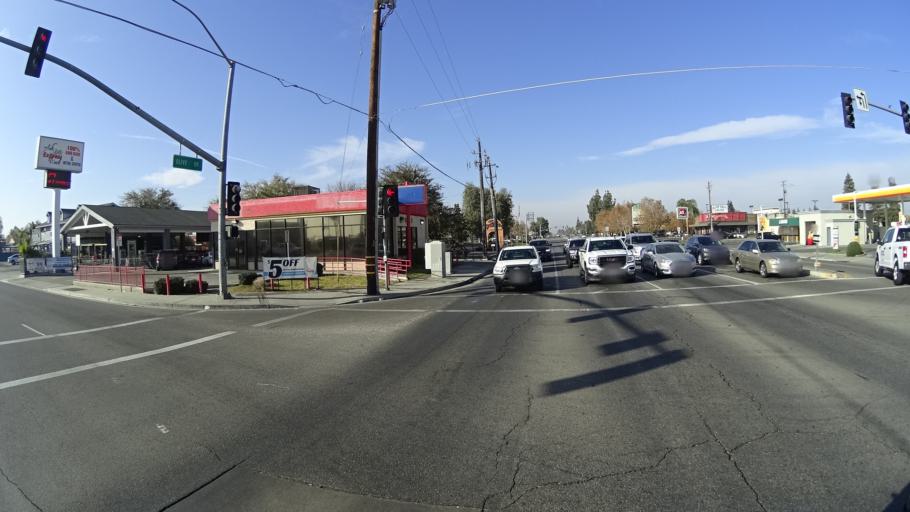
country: US
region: California
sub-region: Kern County
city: Oildale
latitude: 35.4122
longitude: -119.0587
